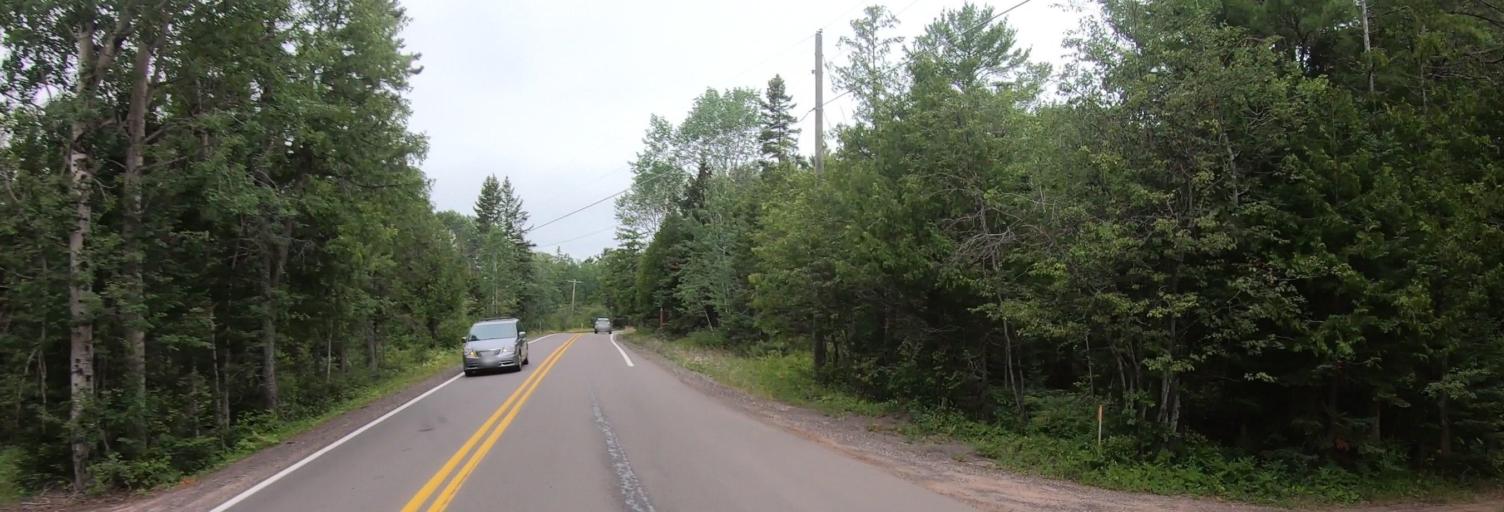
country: US
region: Michigan
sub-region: Keweenaw County
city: Eagle River
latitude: 47.4567
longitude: -88.1425
